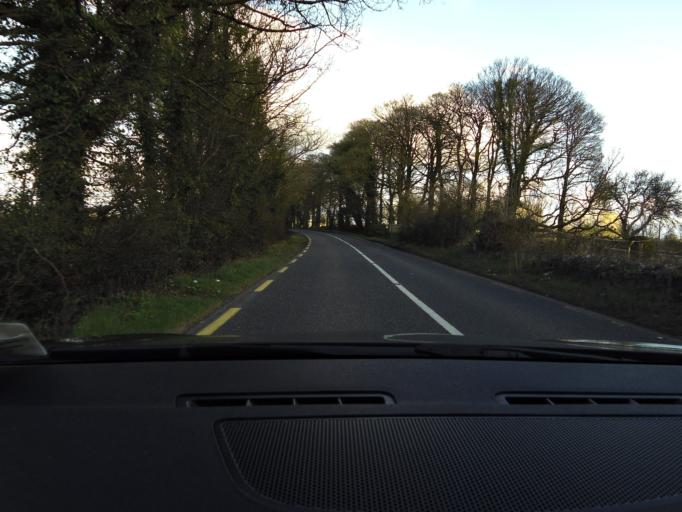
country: IE
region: Connaught
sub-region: Roscommon
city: Roscommon
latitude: 53.6696
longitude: -8.3343
